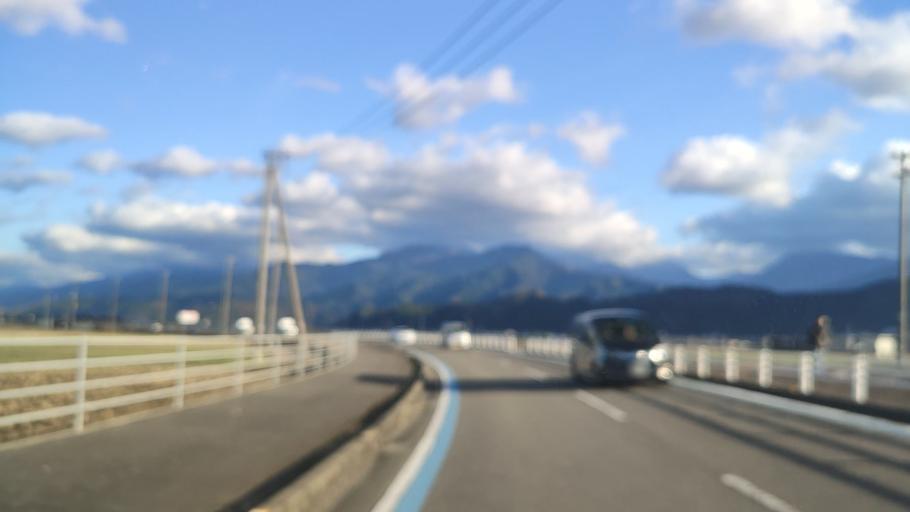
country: JP
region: Ehime
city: Saijo
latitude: 33.9073
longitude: 133.1434
